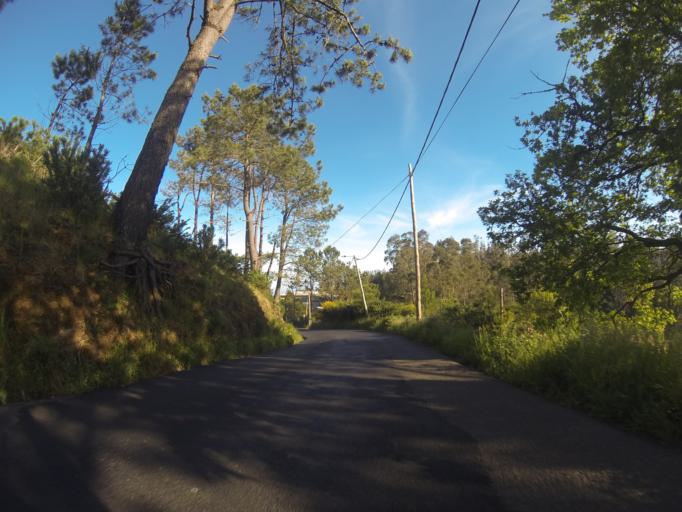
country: PT
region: Madeira
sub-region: Santa Cruz
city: Camacha
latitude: 32.6789
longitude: -16.8697
